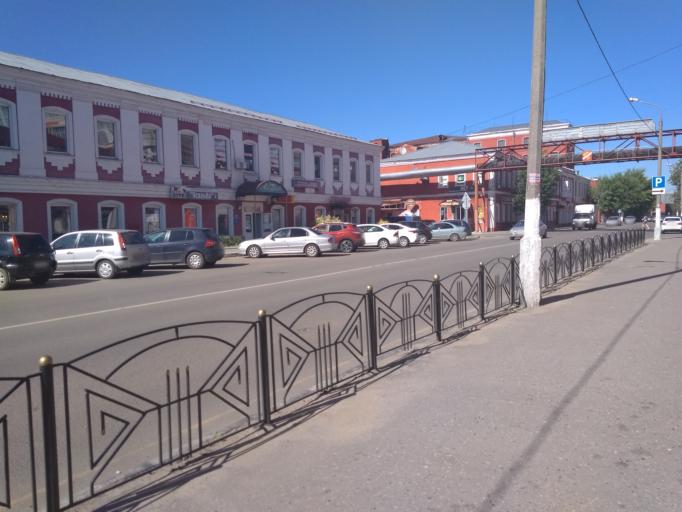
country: RU
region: Moskovskaya
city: Orekhovo-Zuyevo
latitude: 55.8067
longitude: 38.9873
